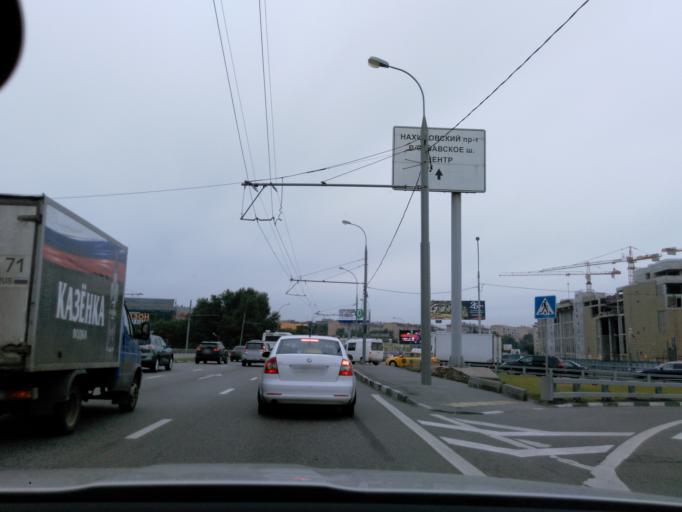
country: RU
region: Moscow
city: Nagornyy
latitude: 55.6626
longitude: 37.6326
